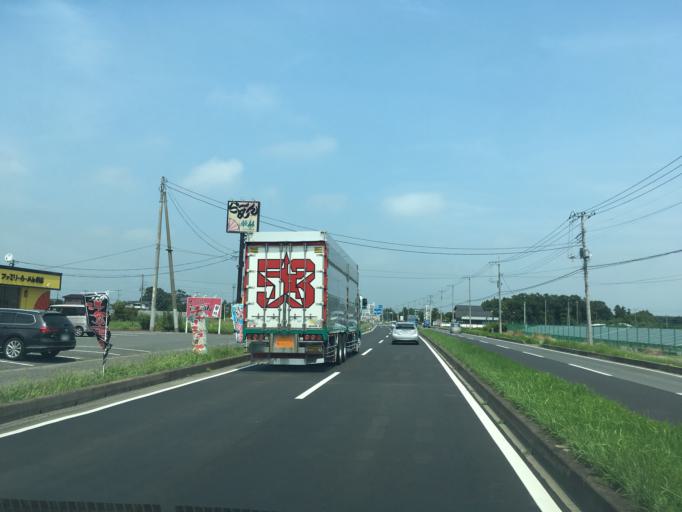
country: JP
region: Ibaraki
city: Hitachi-Naka
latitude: 36.3942
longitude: 140.5805
